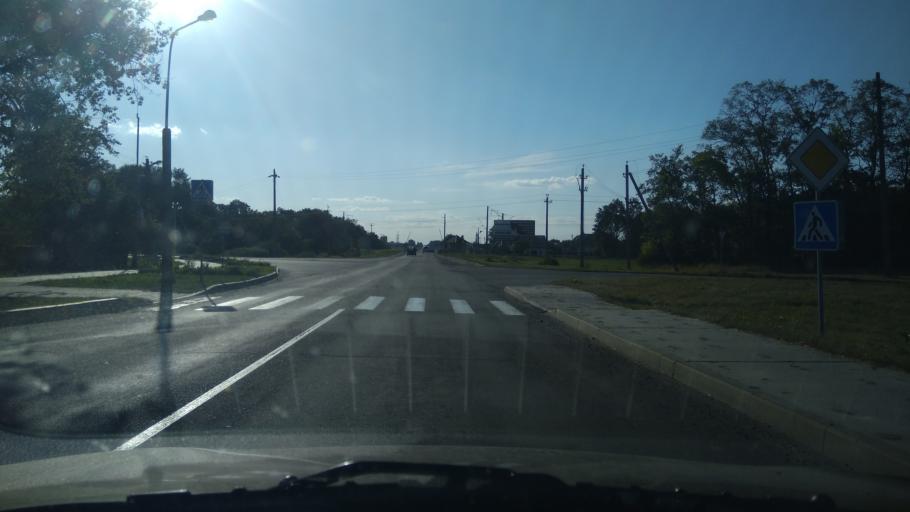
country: BY
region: Brest
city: Byaroza
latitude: 52.5445
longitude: 24.9630
